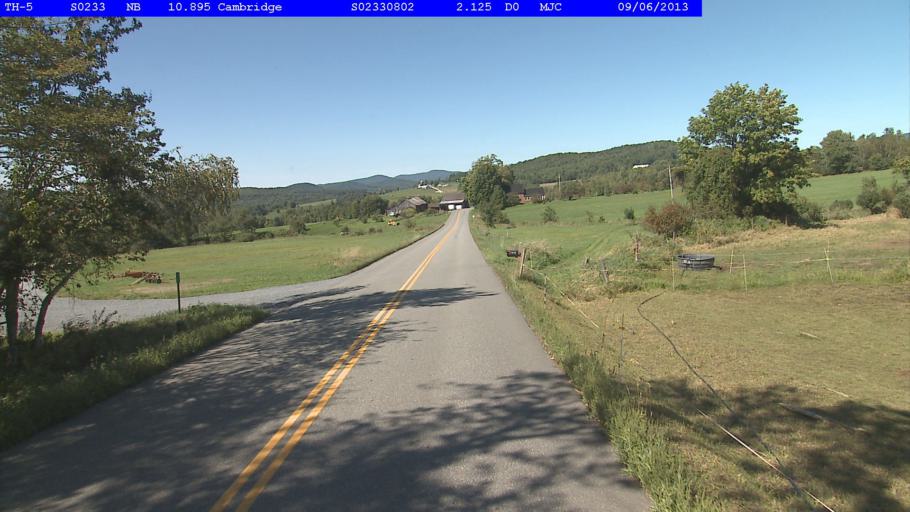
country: US
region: Vermont
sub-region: Chittenden County
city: Jericho
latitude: 44.6124
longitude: -72.8569
